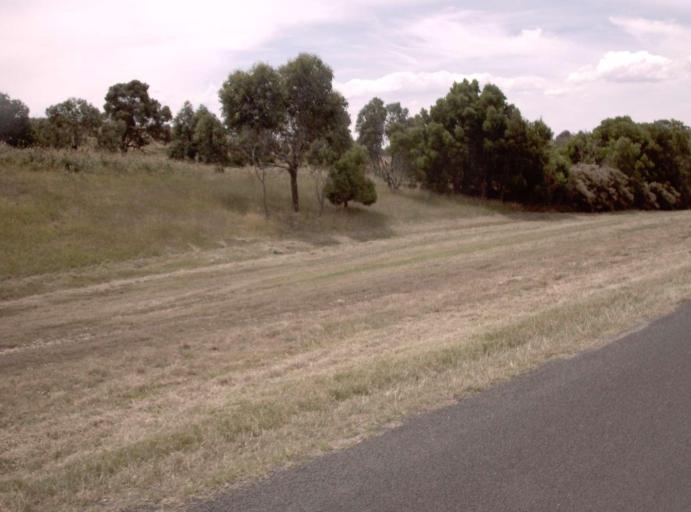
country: AU
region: Victoria
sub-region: Mornington Peninsula
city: Mount Martha
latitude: -38.2786
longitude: 145.0565
